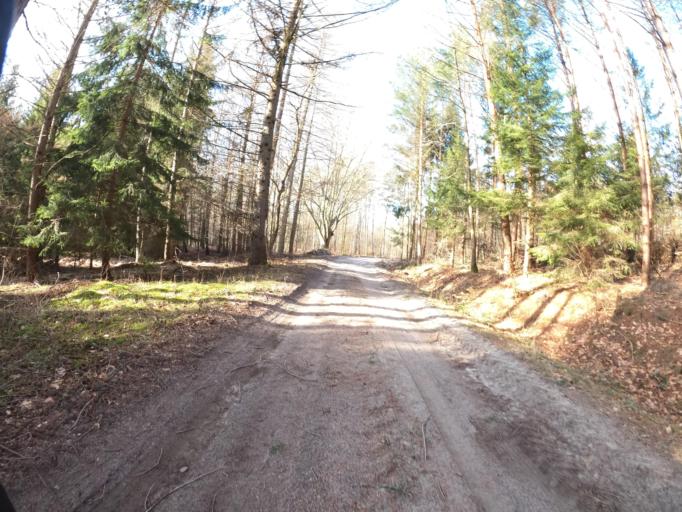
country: PL
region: West Pomeranian Voivodeship
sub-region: Powiat koszalinski
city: Polanow
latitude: 54.2358
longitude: 16.6750
